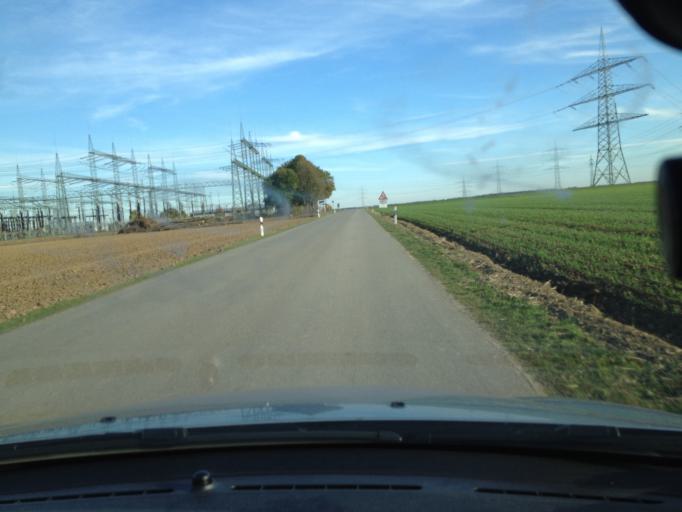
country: DE
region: Bavaria
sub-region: Swabia
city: Oberottmarshausen
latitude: 48.2374
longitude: 10.8358
